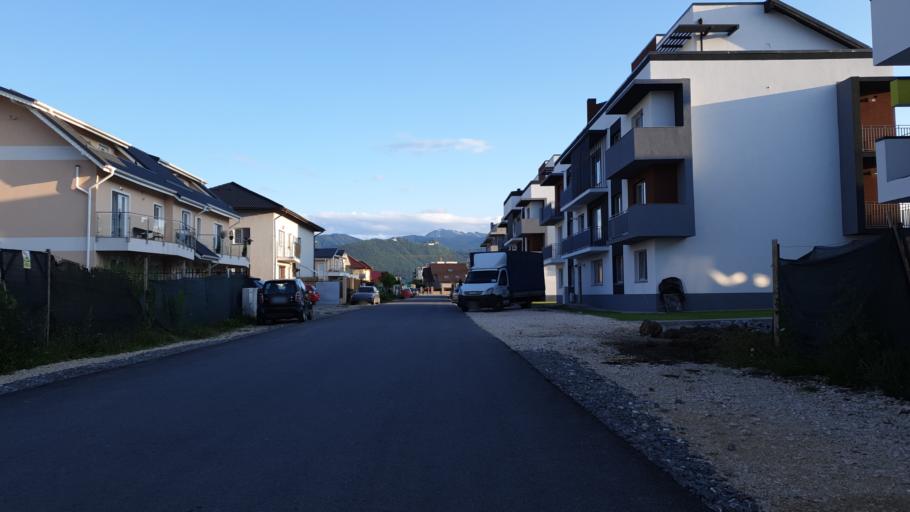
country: RO
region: Brasov
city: Brasov
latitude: 45.6788
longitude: 25.6091
